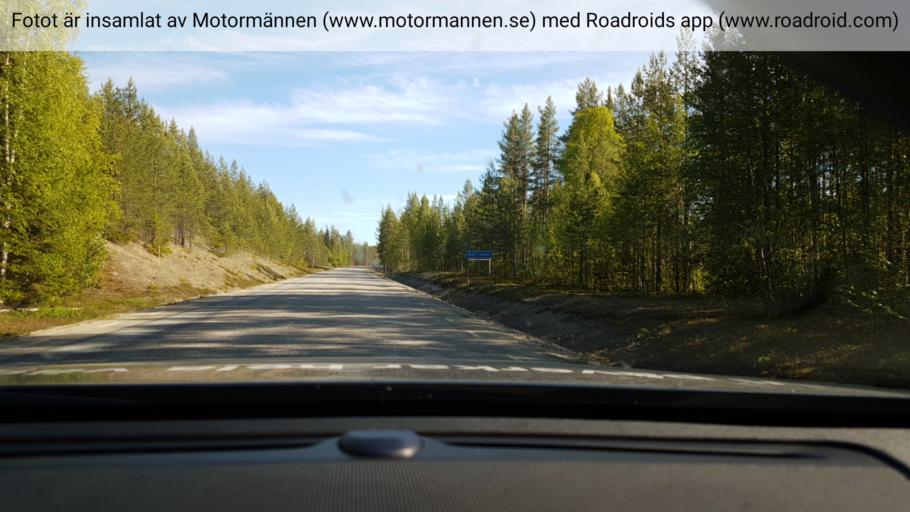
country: SE
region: Vaesterbotten
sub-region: Norsjo Kommun
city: Norsjoe
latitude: 64.6084
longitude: 19.2953
